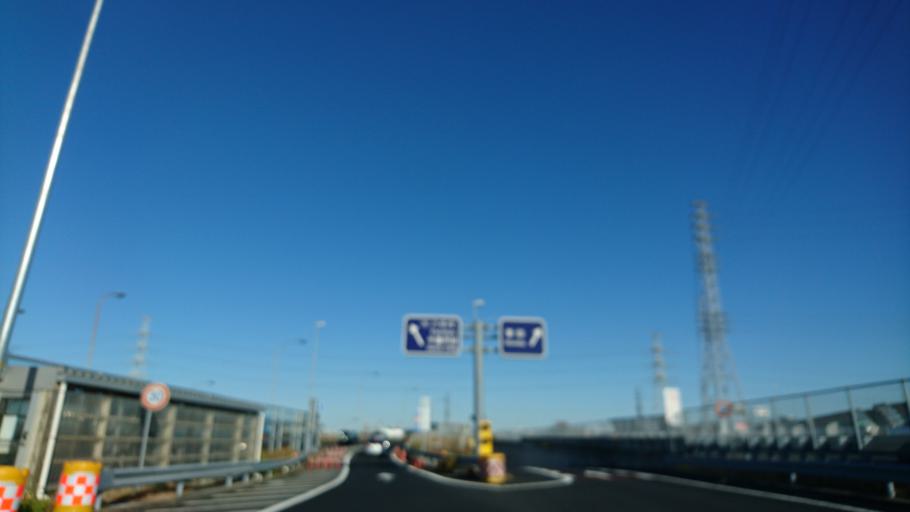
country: JP
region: Chiba
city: Chiba
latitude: 35.5619
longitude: 140.1383
